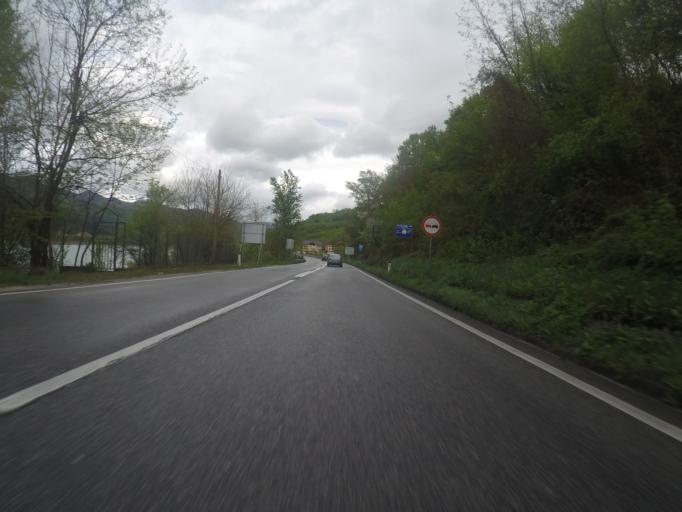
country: BA
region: Federation of Bosnia and Herzegovina
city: Jablanica
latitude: 43.6938
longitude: 17.8466
